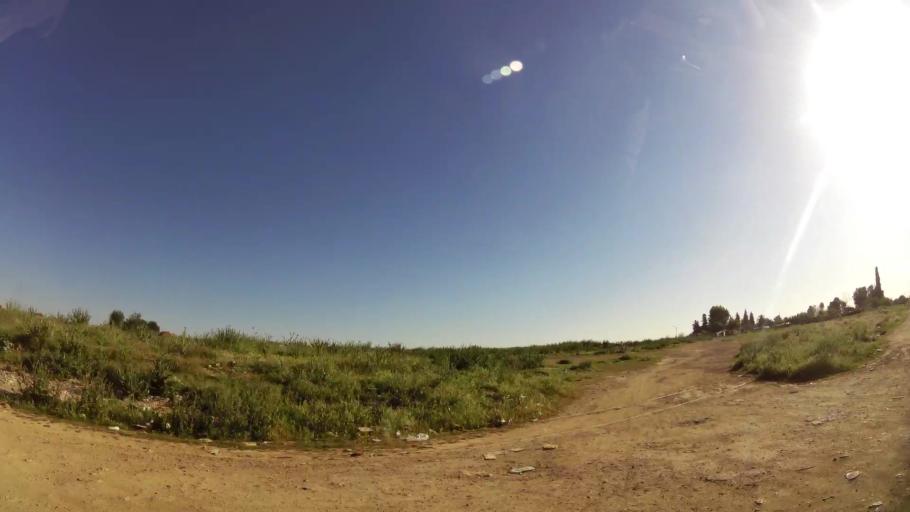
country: MA
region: Meknes-Tafilalet
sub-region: Meknes
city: Meknes
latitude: 33.8886
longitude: -5.5094
